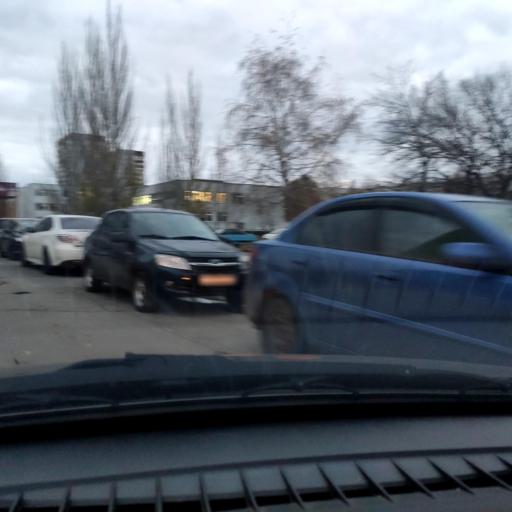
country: RU
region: Samara
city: Tol'yatti
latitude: 53.5392
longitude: 49.3362
